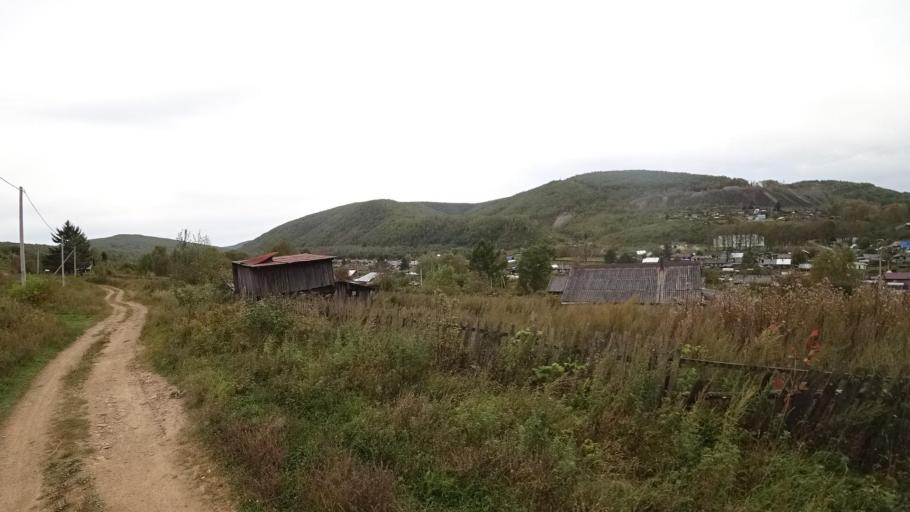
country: RU
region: Jewish Autonomous Oblast
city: Khingansk
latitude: 49.1272
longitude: 131.2039
